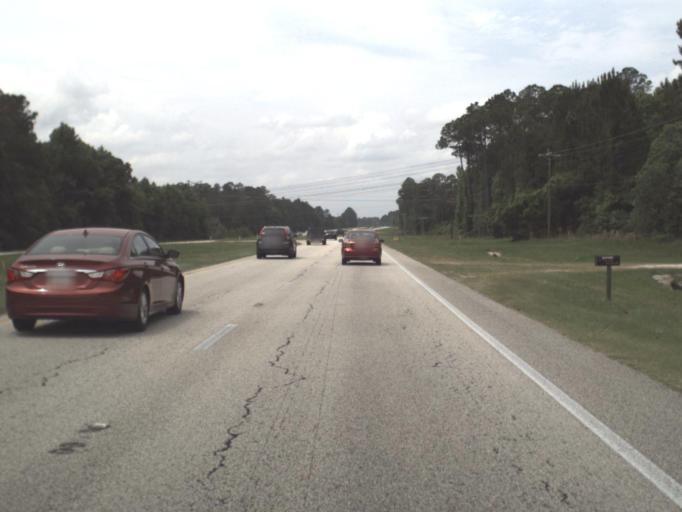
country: US
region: Florida
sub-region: Clay County
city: Middleburg
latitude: 30.0994
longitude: -81.8369
